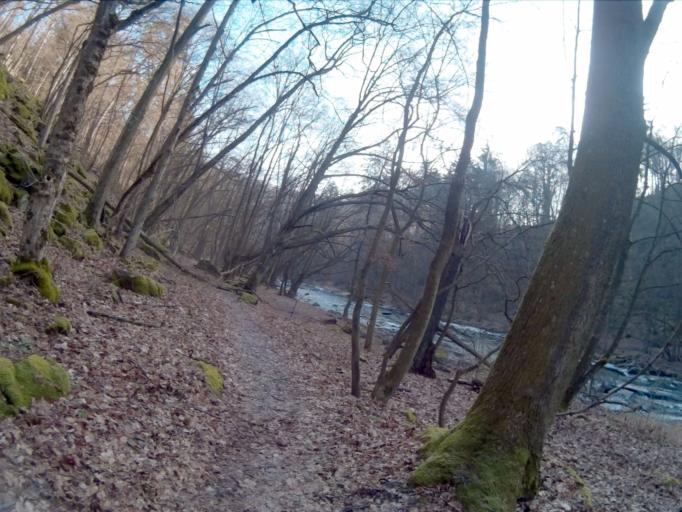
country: CZ
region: Vysocina
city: Namest' nad Oslavou
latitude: 49.1759
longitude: 16.1598
